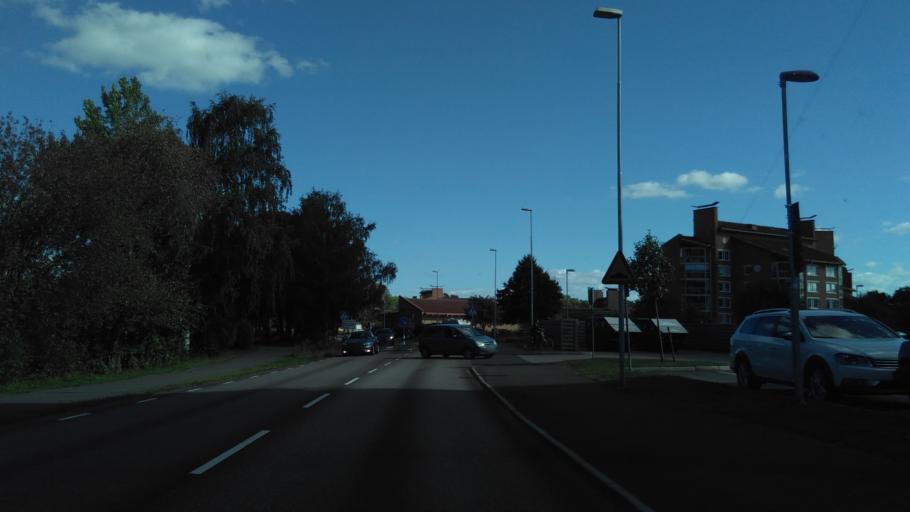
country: SE
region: Vaestra Goetaland
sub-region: Skovde Kommun
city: Skoevde
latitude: 58.4011
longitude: 13.8365
